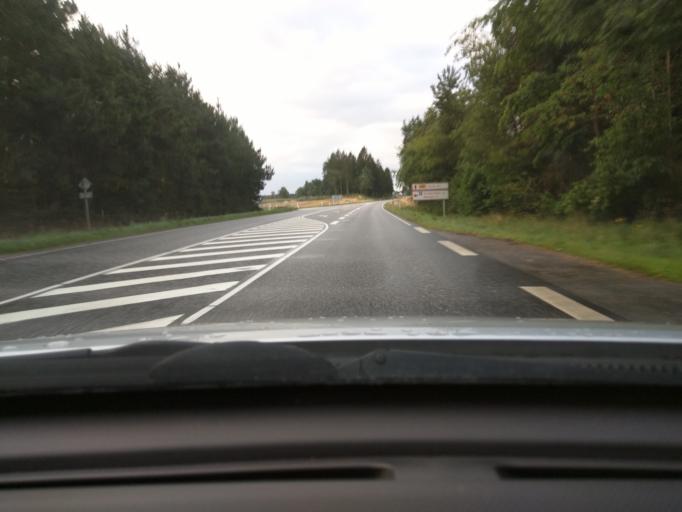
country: DK
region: Central Jutland
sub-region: Ikast-Brande Kommune
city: Bording Kirkeby
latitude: 56.2528
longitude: 9.3201
